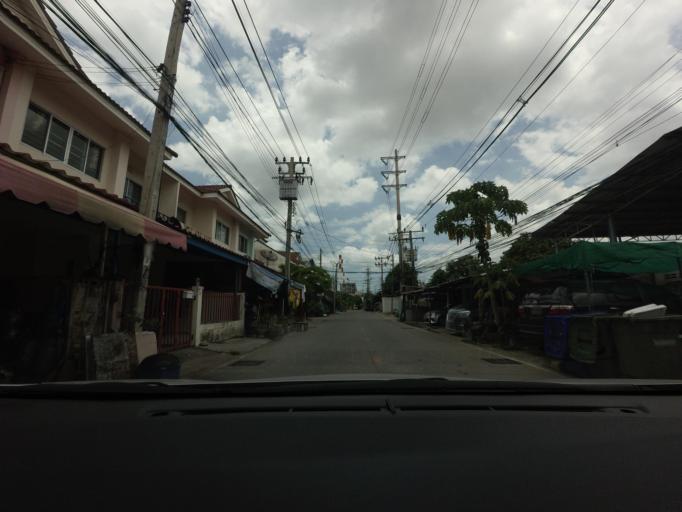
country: TH
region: Samut Prakan
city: Phra Samut Chedi
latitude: 13.6244
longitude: 100.5614
